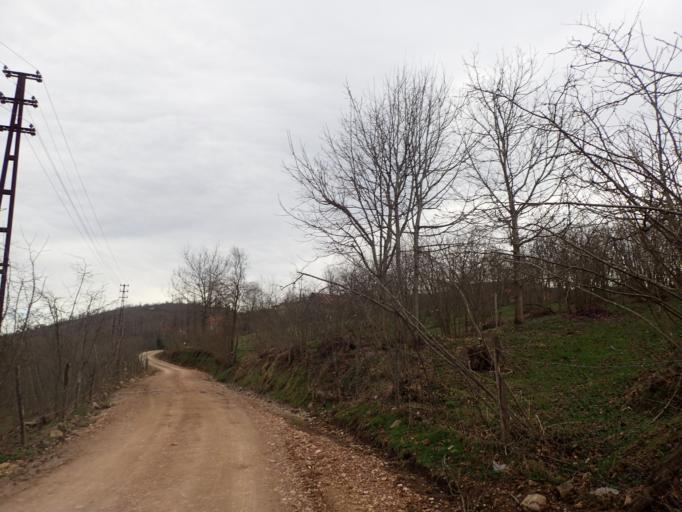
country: TR
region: Ordu
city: Camas
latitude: 40.8902
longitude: 37.5189
